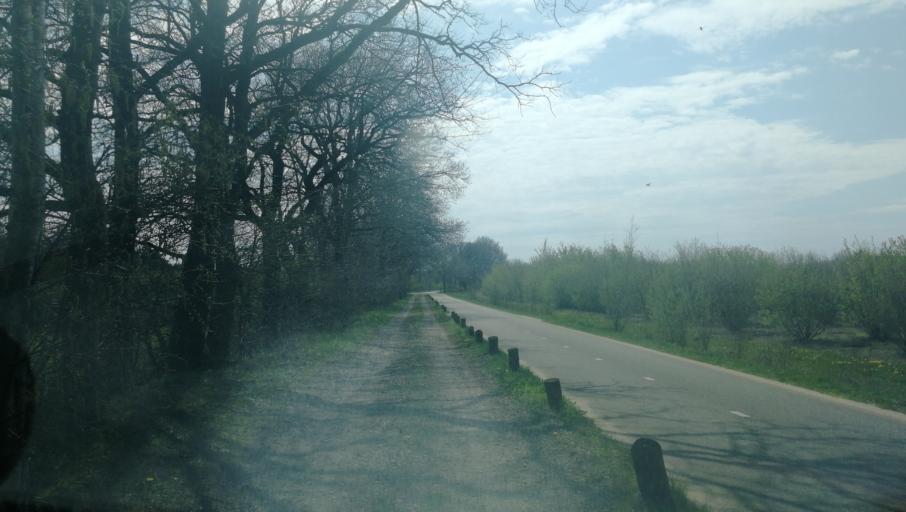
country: NL
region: Limburg
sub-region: Gemeente Venlo
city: Tegelen
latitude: 51.4023
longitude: 6.1003
